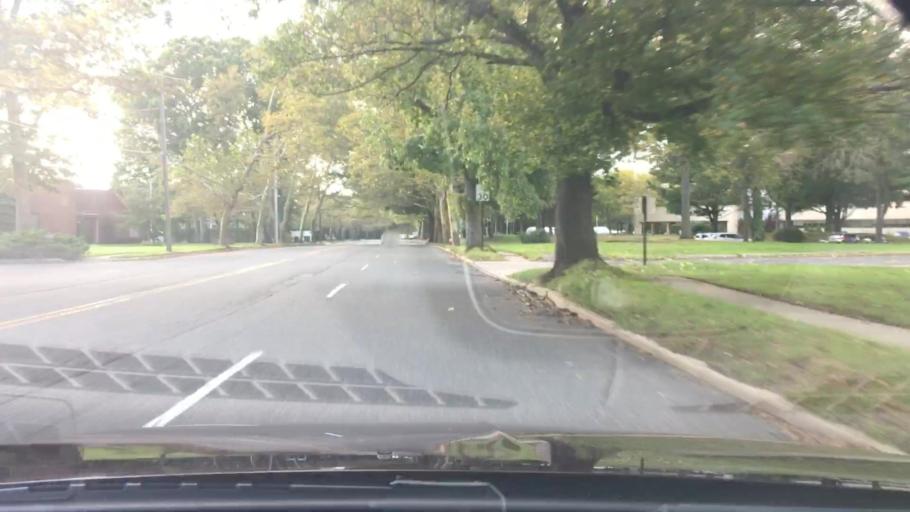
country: US
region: New York
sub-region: Suffolk County
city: Melville
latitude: 40.7685
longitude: -73.4093
